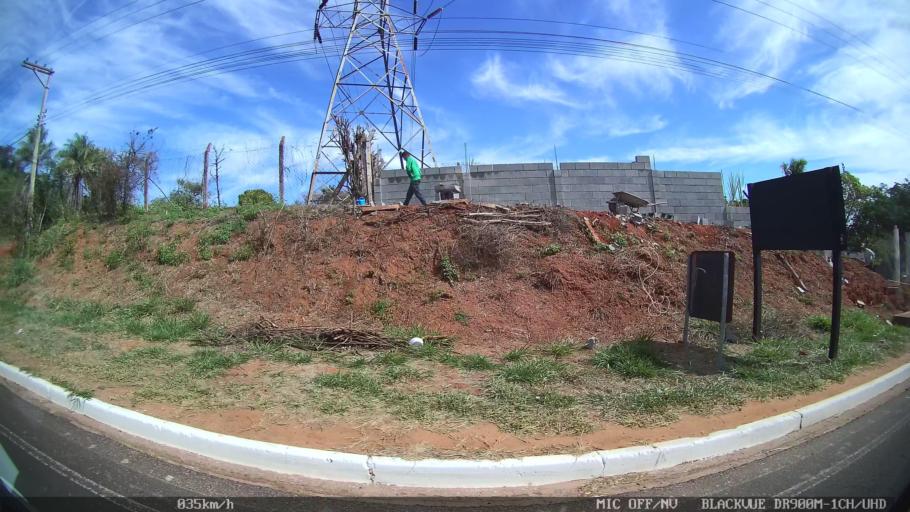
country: BR
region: Sao Paulo
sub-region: Sao Jose Do Rio Preto
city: Sao Jose do Rio Preto
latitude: -20.8282
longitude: -49.3435
